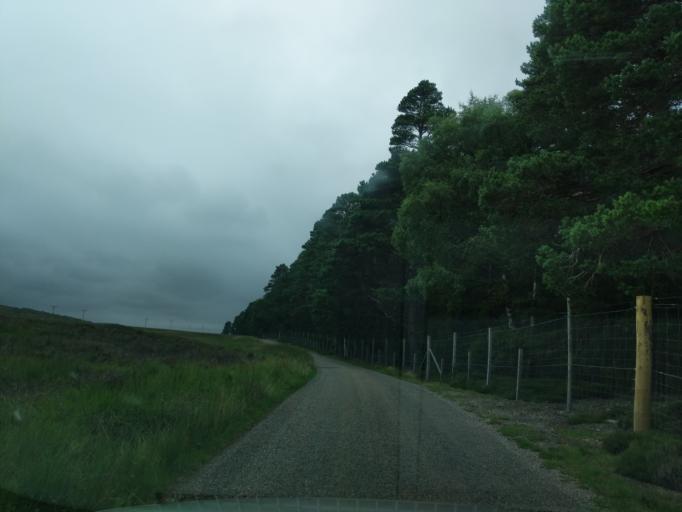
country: GB
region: Scotland
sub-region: Highland
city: Grantown on Spey
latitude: 57.4004
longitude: -3.7077
